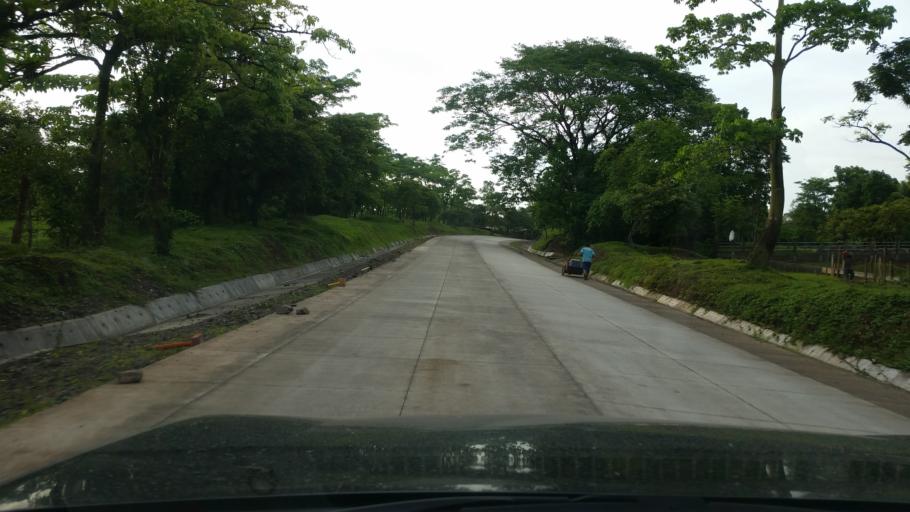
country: NI
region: Matagalpa
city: Rio Blanco
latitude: 13.1002
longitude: -85.0659
